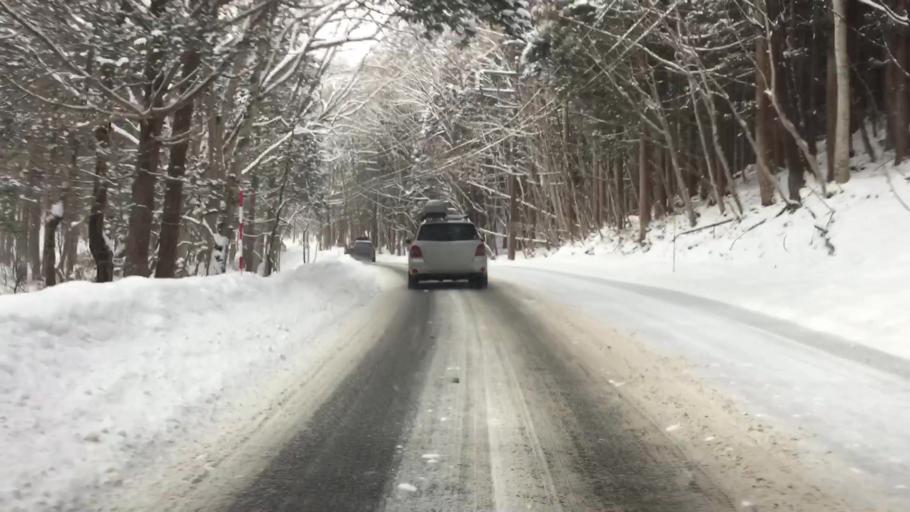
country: JP
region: Tochigi
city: Yaita
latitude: 36.9539
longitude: 139.7608
